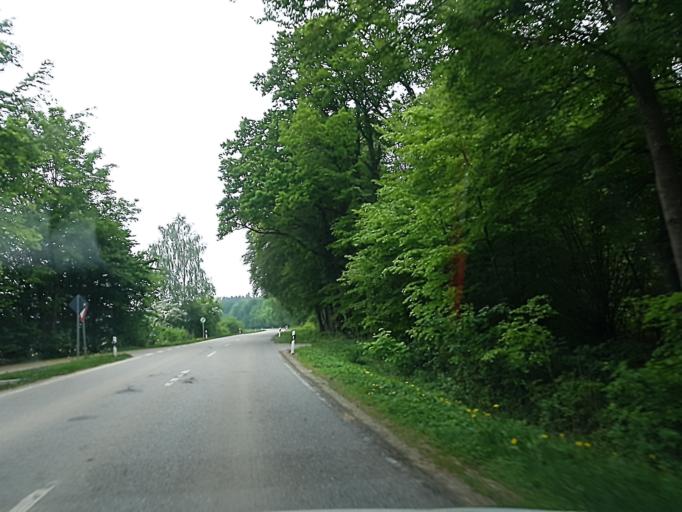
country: DE
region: Bavaria
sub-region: Upper Bavaria
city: Ebersberg
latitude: 48.0986
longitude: 11.9777
